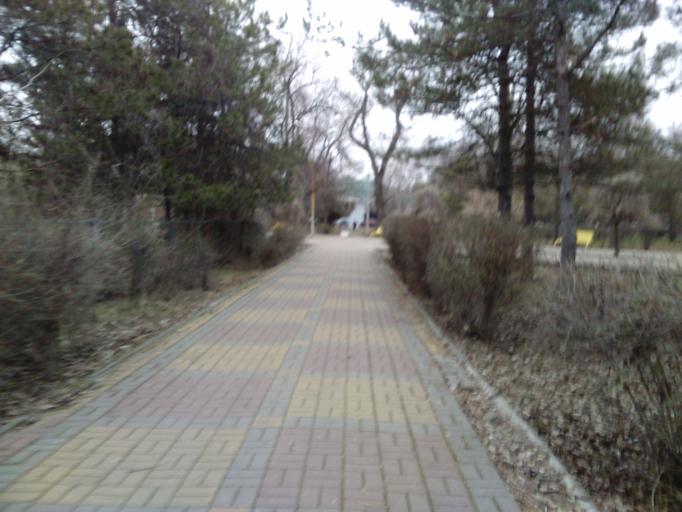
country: RU
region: Rostov
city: Bataysk
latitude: 47.1356
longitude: 39.7425
